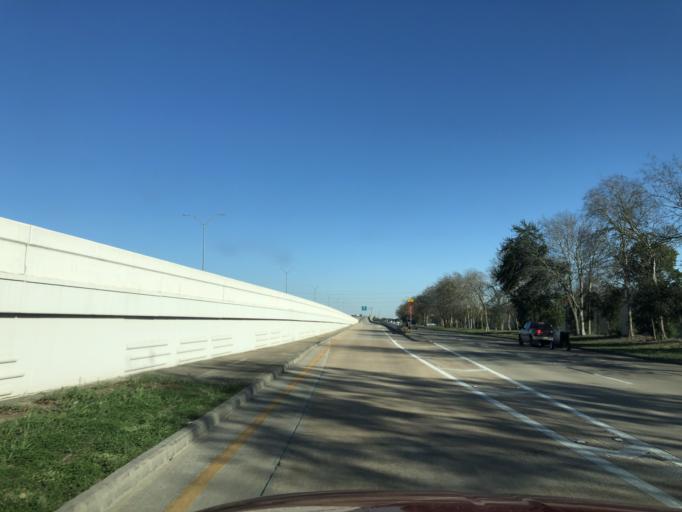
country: US
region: Texas
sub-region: Fort Bend County
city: Fresno
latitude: 29.5963
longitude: -95.4532
